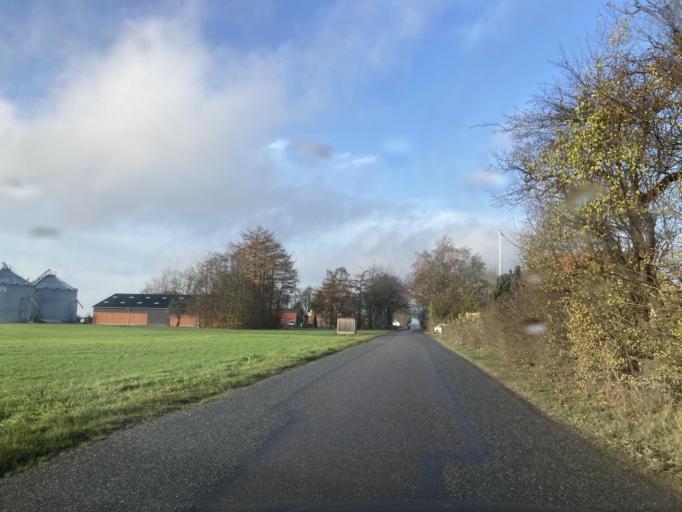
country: DK
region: Zealand
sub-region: Lolland Kommune
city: Rodby
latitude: 54.6792
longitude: 11.4218
